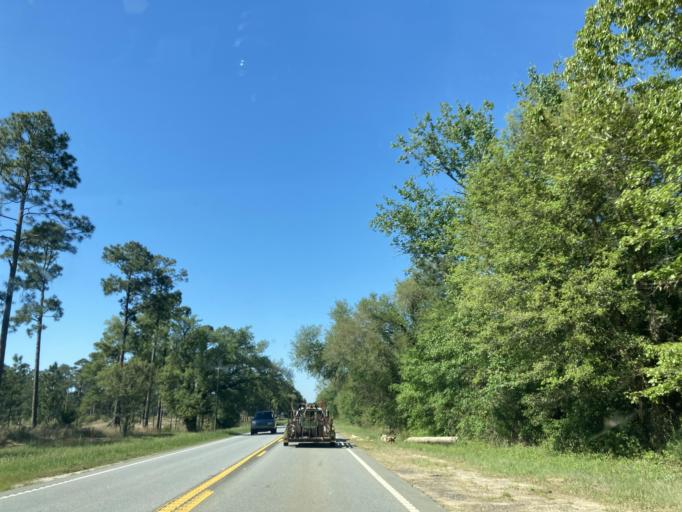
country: US
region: Georgia
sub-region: Baker County
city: Newton
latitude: 31.4047
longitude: -84.2765
